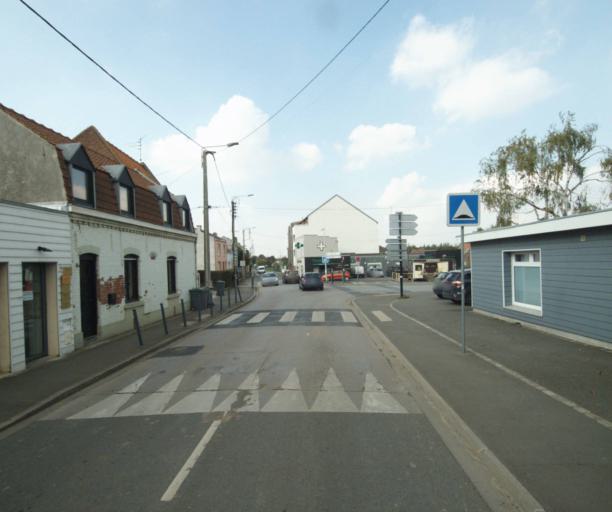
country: FR
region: Nord-Pas-de-Calais
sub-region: Departement du Nord
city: Houplin-Ancoisne
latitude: 50.5733
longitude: 2.9963
